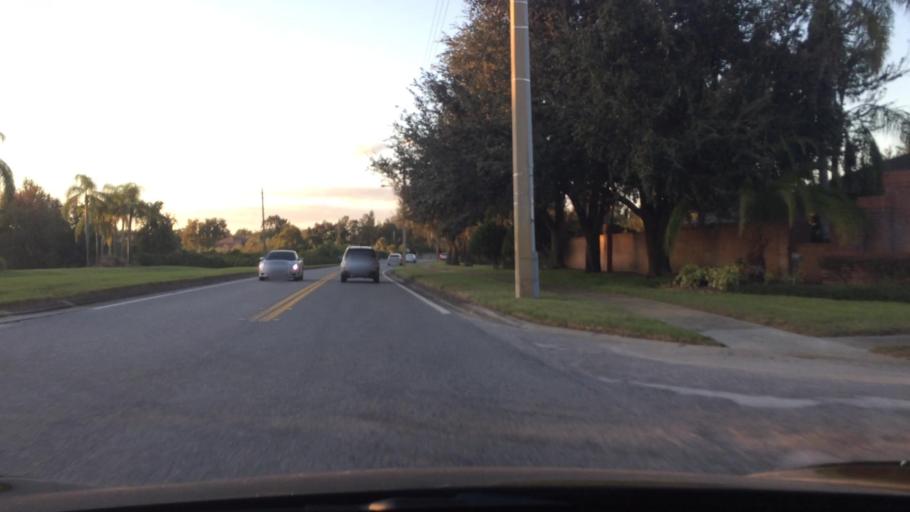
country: US
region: Florida
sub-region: Hillsborough County
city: Lutz
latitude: 28.1765
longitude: -82.4390
